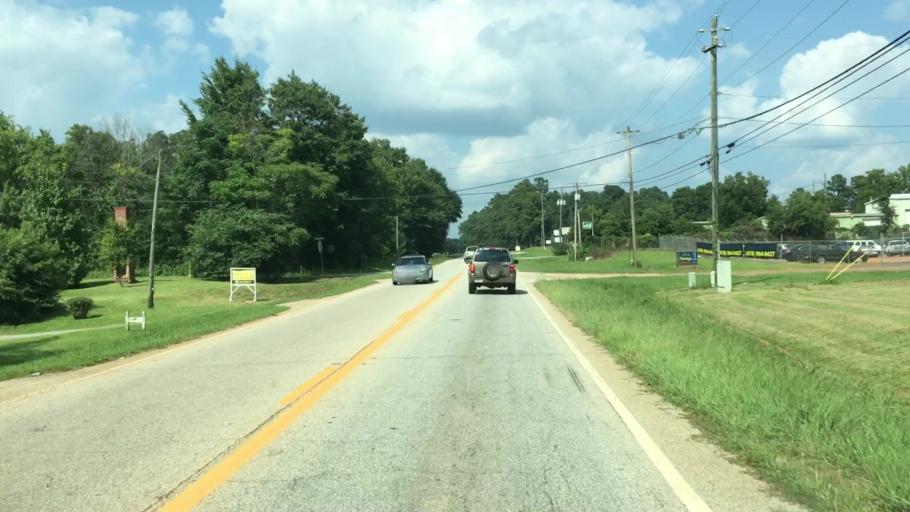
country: US
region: Georgia
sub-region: Monroe County
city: Forsyth
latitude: 33.0507
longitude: -83.9309
